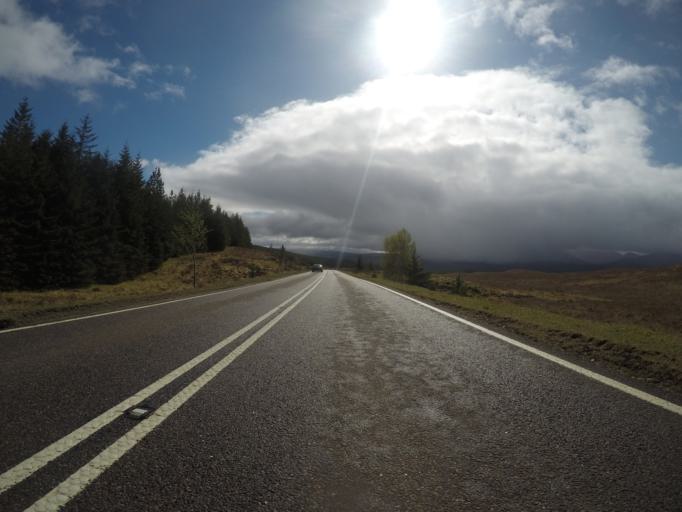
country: GB
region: Scotland
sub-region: Highland
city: Spean Bridge
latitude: 57.0942
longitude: -4.9930
